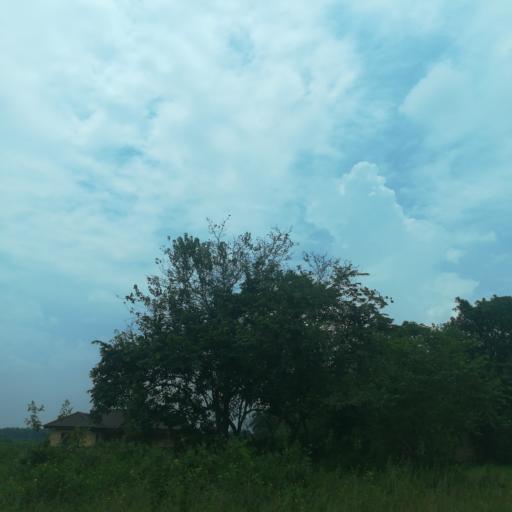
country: NG
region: Lagos
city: Ejirin
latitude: 6.6788
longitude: 3.7997
